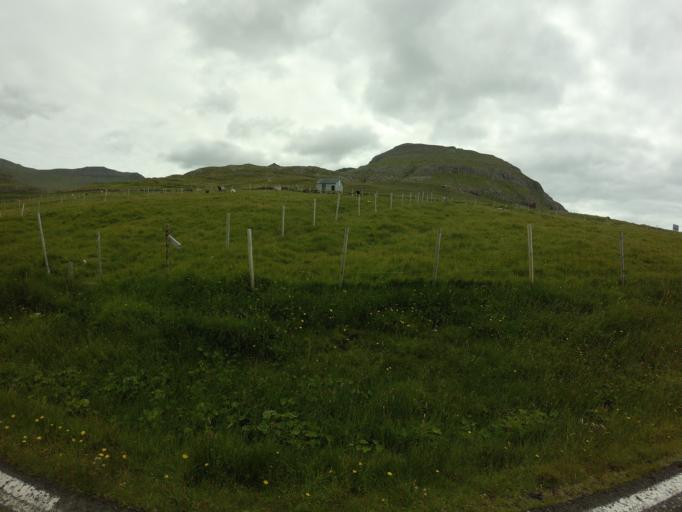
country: FO
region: Suduroy
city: Tvoroyri
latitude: 61.5196
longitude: -6.8884
